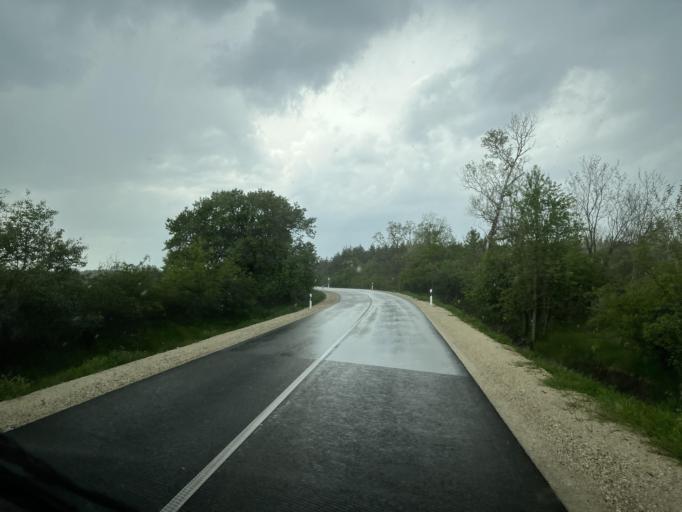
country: HU
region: Pest
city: Csemo
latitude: 47.0751
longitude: 19.6865
